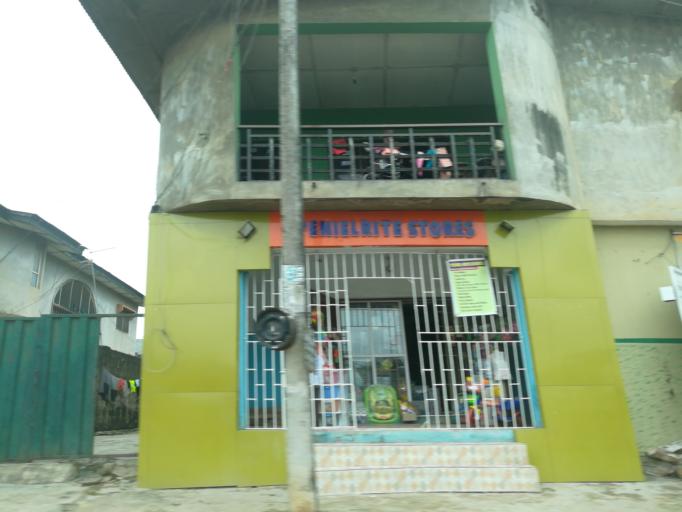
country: NG
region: Lagos
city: Ojota
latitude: 6.6161
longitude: 3.3974
